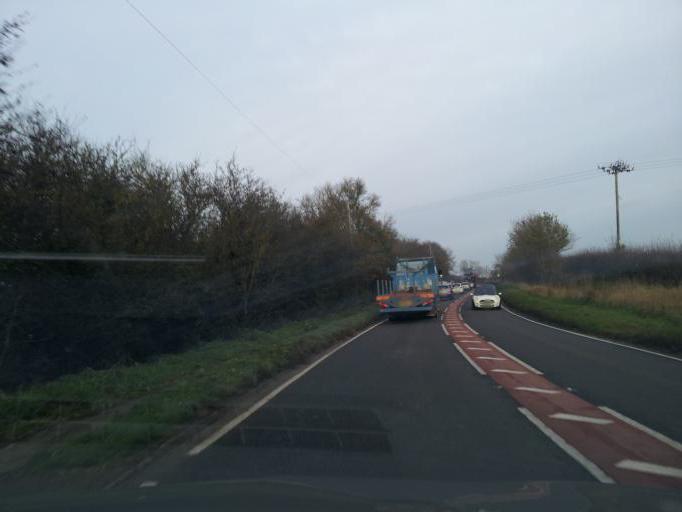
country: GB
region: England
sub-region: Buckinghamshire
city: Stewkley
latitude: 51.8872
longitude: -0.7290
